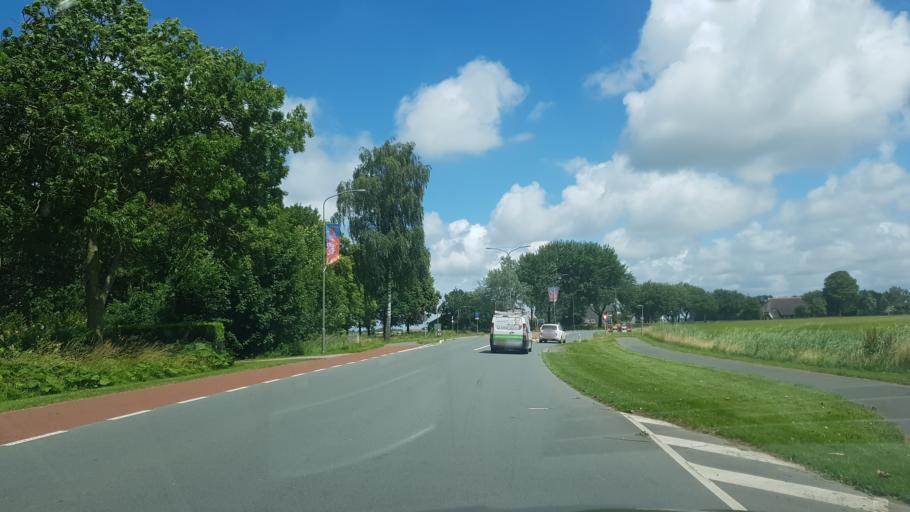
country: NL
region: Groningen
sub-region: Gemeente Winsum
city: Winsum
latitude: 53.3982
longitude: 6.5664
